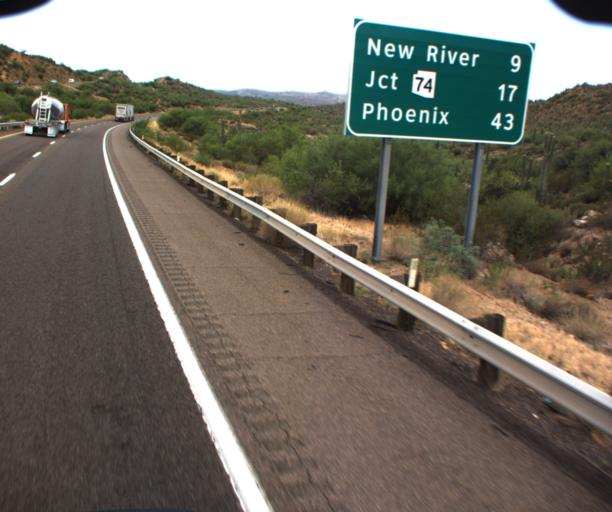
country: US
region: Arizona
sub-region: Yavapai County
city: Black Canyon City
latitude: 34.0334
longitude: -112.1466
